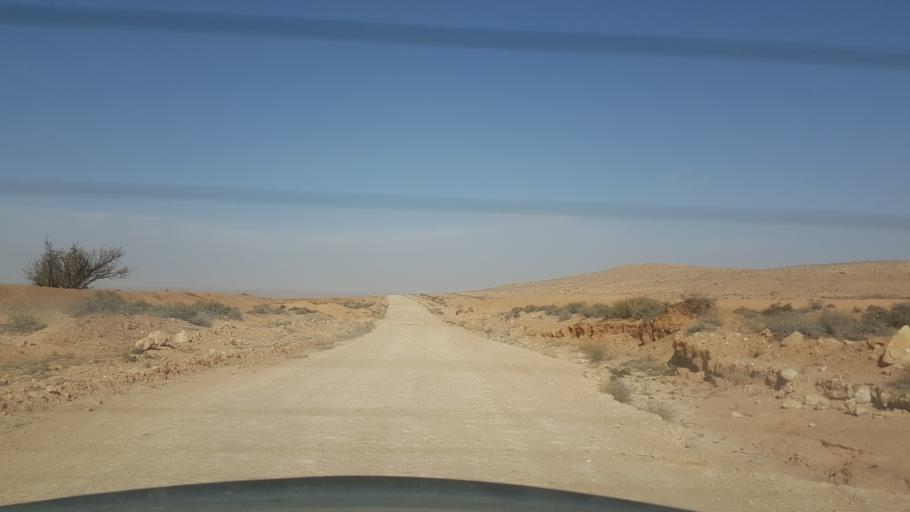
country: TN
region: Qabis
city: El Hamma
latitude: 33.6539
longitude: 9.7359
